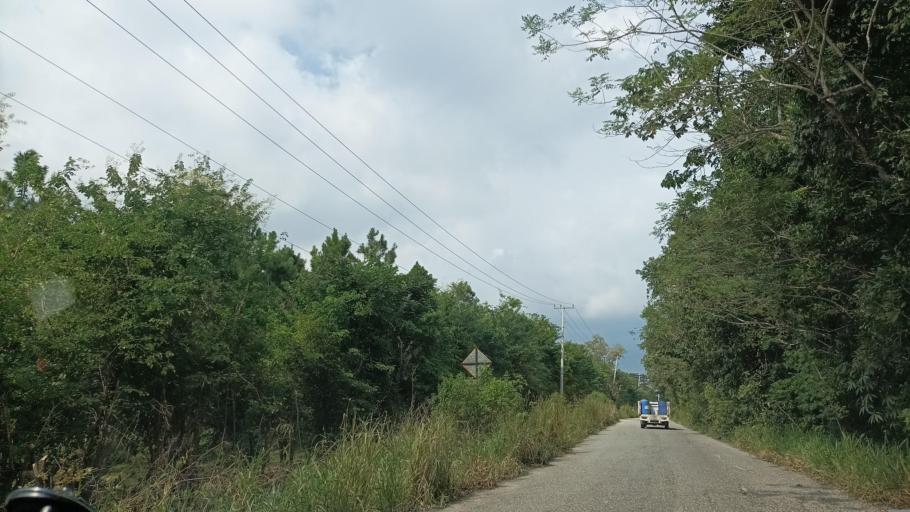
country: MX
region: Veracruz
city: Las Choapas
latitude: 17.8040
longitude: -94.1077
